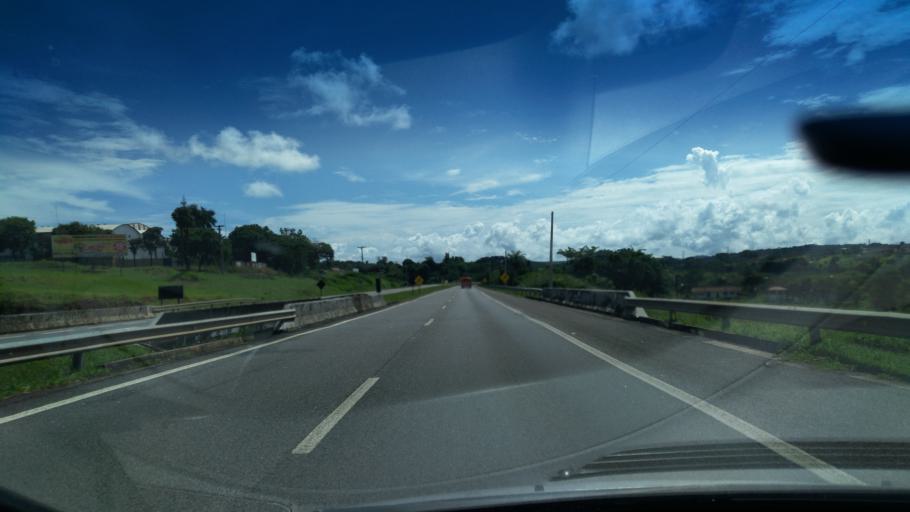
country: BR
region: Sao Paulo
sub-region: Santo Antonio Do Jardim
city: Espirito Santo do Pinhal
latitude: -22.2040
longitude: -46.7778
